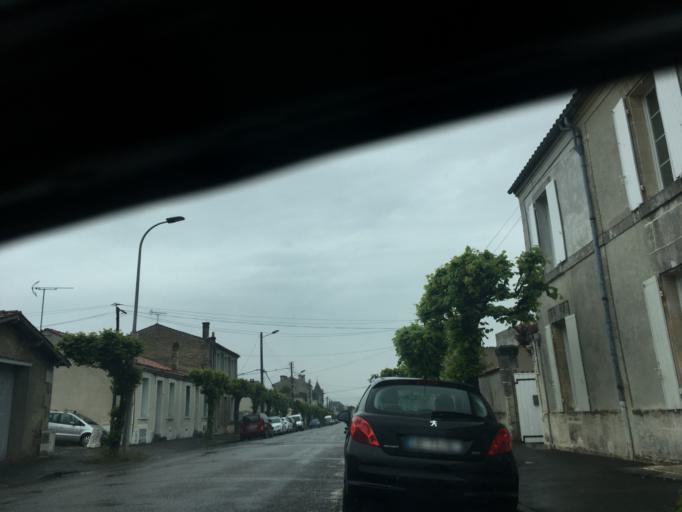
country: FR
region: Poitou-Charentes
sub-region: Departement de la Charente
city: Cognac
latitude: 45.6873
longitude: -0.3228
